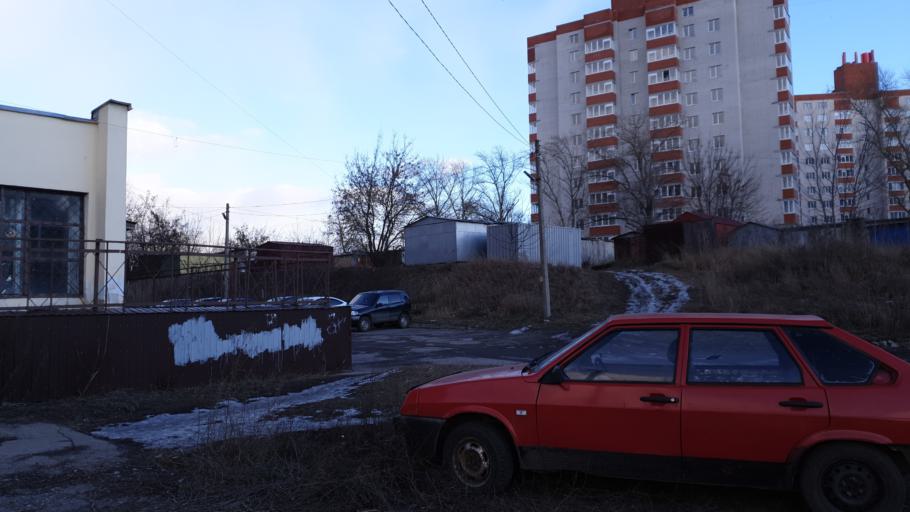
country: RU
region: Kursk
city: Kursk
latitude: 51.7270
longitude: 36.1480
